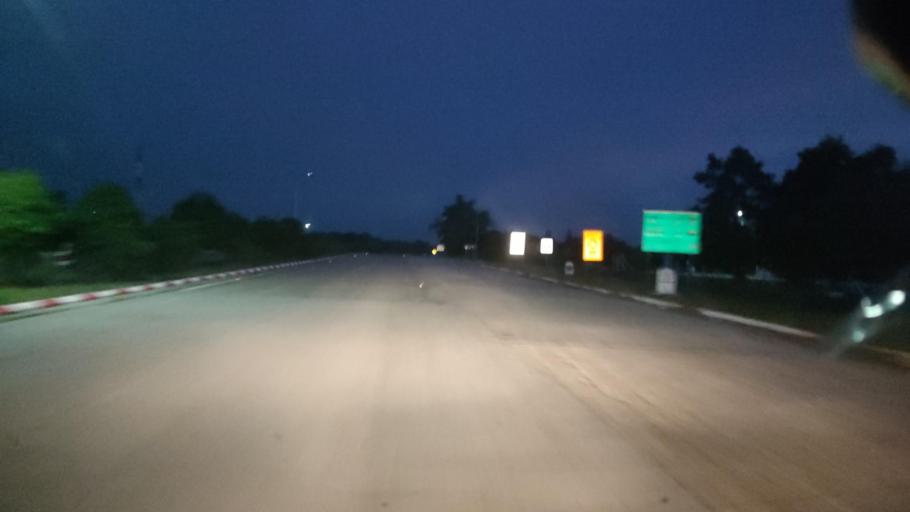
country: MM
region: Mandalay
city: Nay Pyi Taw
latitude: 19.9287
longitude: 95.9879
